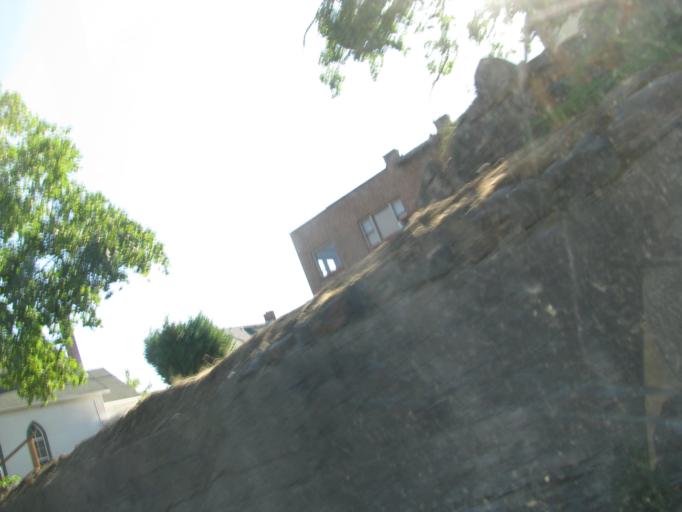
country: US
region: Washington
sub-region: Spokane County
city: Spokane
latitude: 47.6709
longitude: -117.4175
